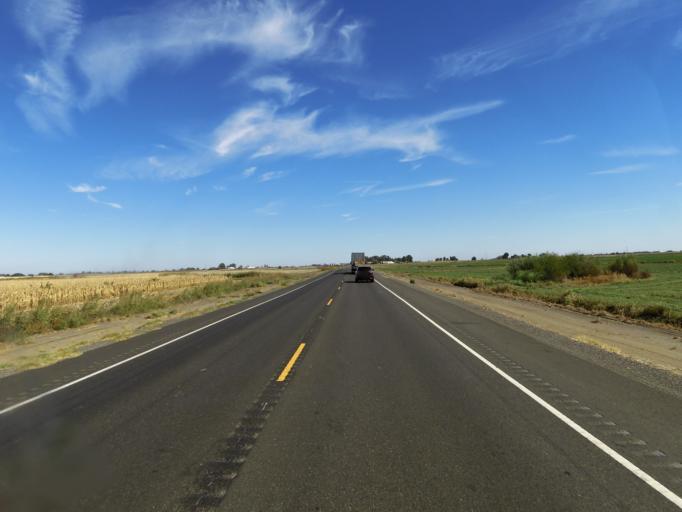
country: US
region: California
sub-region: Solano County
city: Rio Vista
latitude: 38.1442
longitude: -121.6391
